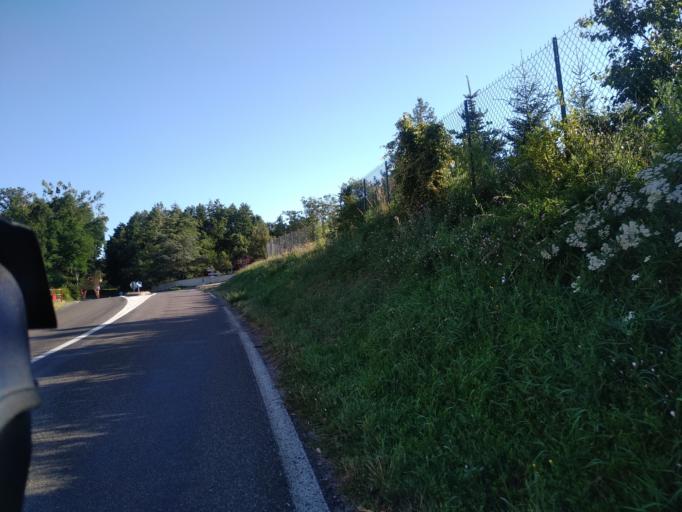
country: FR
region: Rhone-Alpes
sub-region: Departement de la Loire
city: Civens
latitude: 45.7613
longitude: 4.2683
